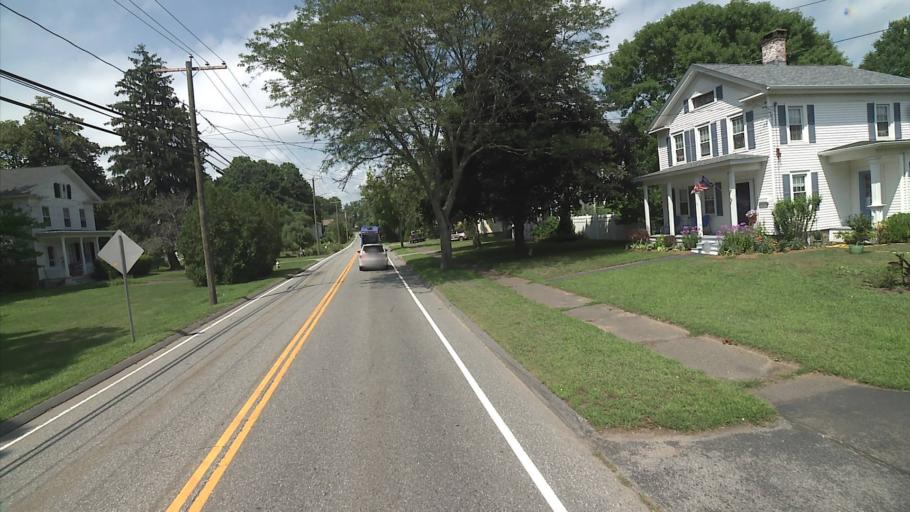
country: US
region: Connecticut
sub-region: Middlesex County
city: Clinton
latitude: 41.2811
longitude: -72.5268
